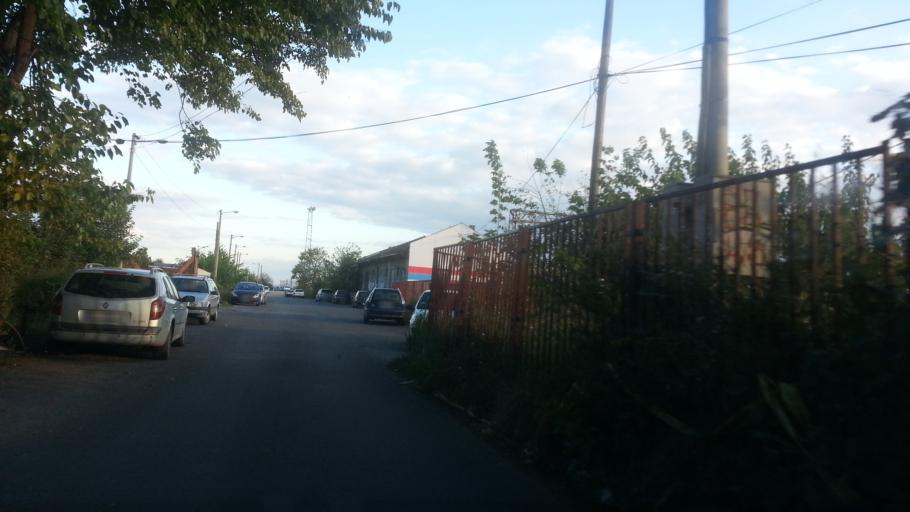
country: RS
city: Novi Banovci
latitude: 44.8988
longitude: 20.2729
